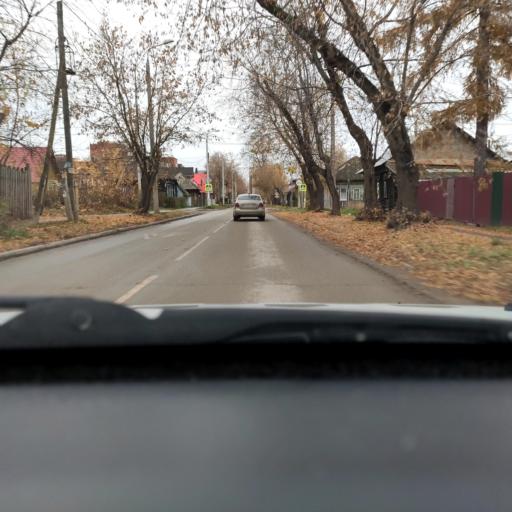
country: RU
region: Perm
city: Perm
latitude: 58.0278
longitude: 56.3309
